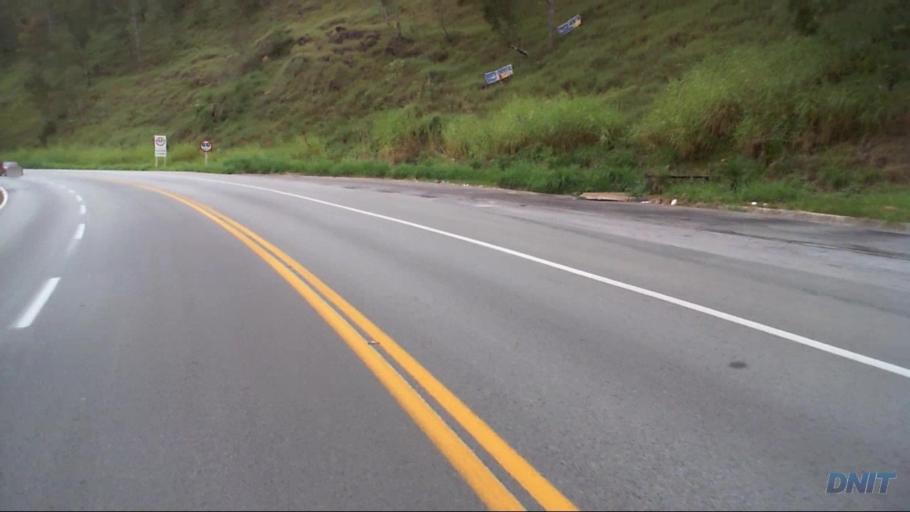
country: BR
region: Minas Gerais
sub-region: Joao Monlevade
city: Joao Monlevade
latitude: -19.8439
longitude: -43.1018
